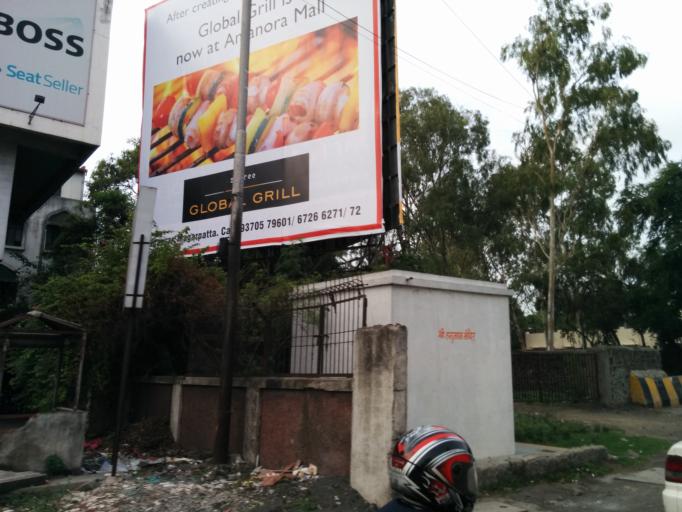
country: IN
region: Maharashtra
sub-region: Pune Division
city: Pune
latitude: 18.5023
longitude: 73.8760
